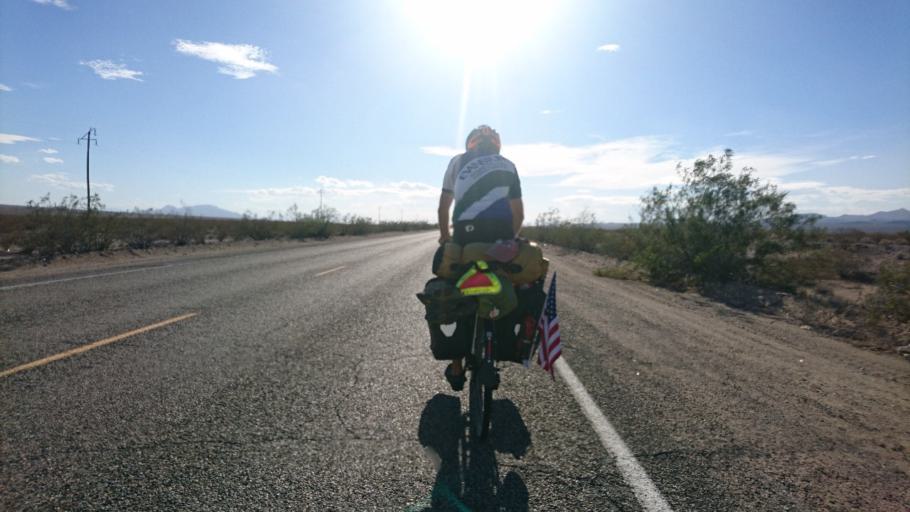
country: US
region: California
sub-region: San Bernardino County
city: Needles
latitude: 34.7134
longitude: -115.2797
